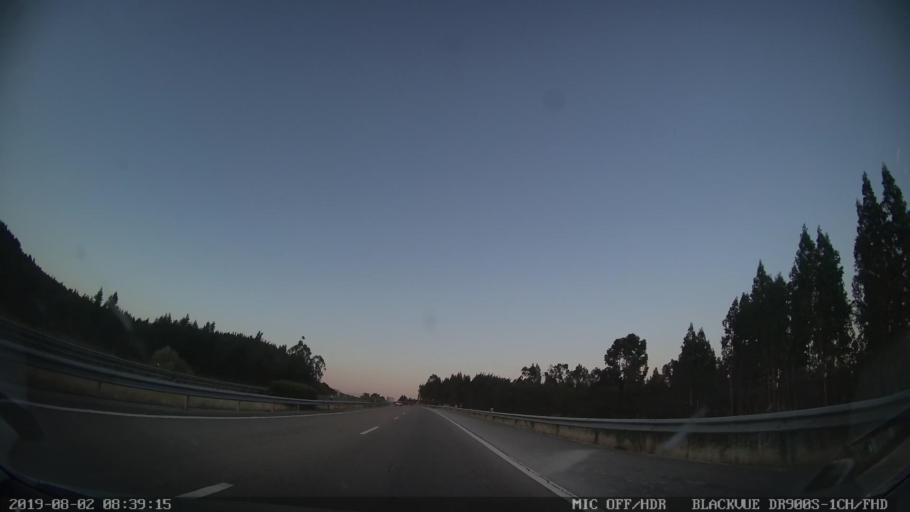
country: PT
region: Santarem
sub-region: Constancia
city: Constancia
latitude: 39.4886
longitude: -8.3162
